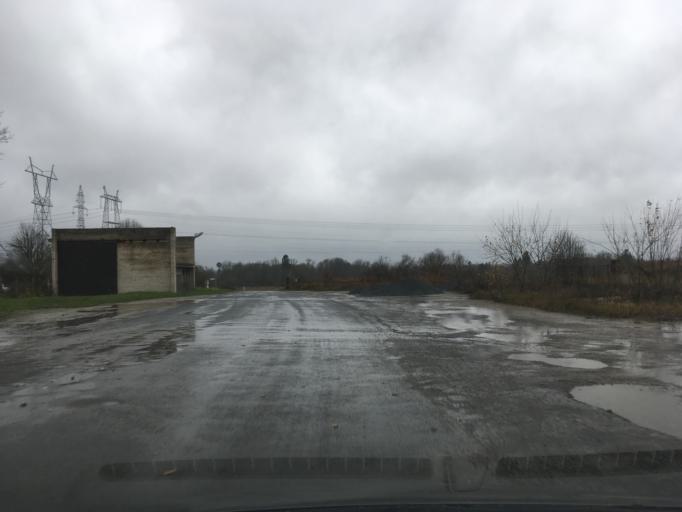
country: EE
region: Laeaene
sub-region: Lihula vald
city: Lihula
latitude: 58.6759
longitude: 23.8217
